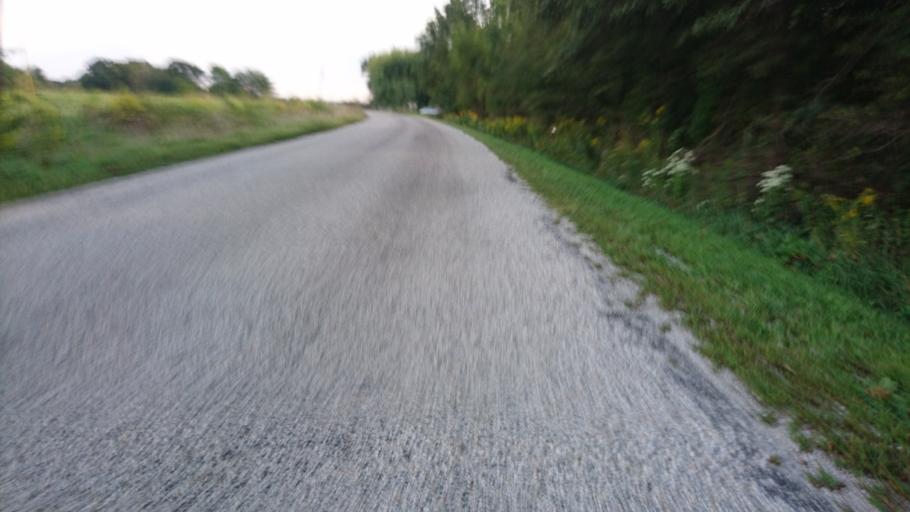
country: US
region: Illinois
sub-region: Logan County
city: Atlanta
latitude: 40.2297
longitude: -89.2045
